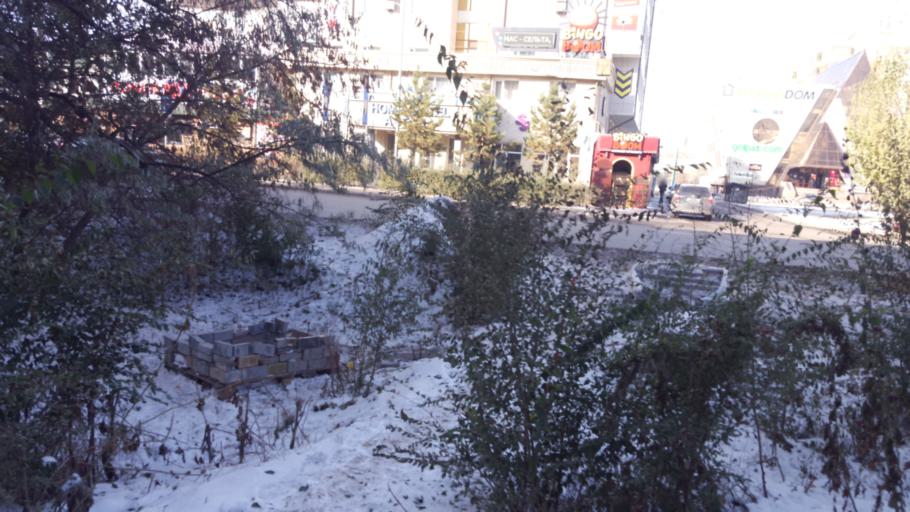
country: KZ
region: Astana Qalasy
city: Astana
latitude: 51.1568
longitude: 71.4889
